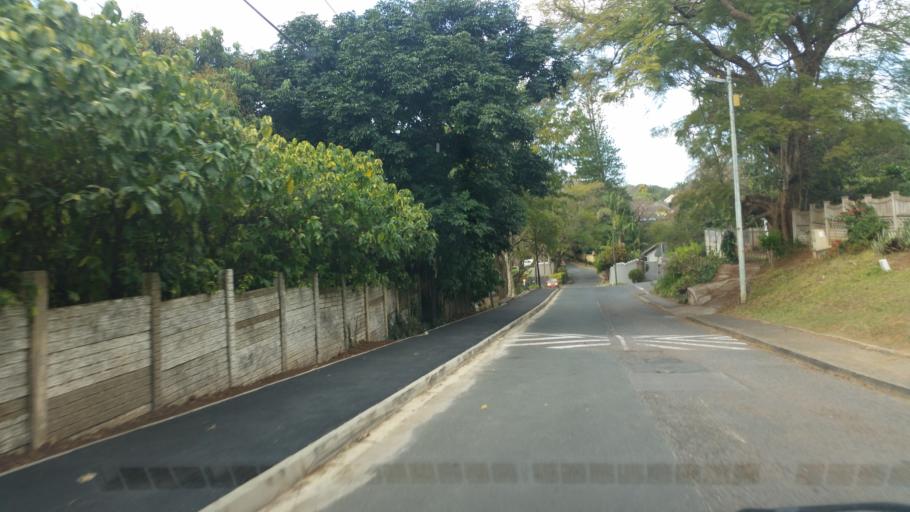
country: ZA
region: KwaZulu-Natal
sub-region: eThekwini Metropolitan Municipality
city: Berea
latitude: -29.8291
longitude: 30.9298
